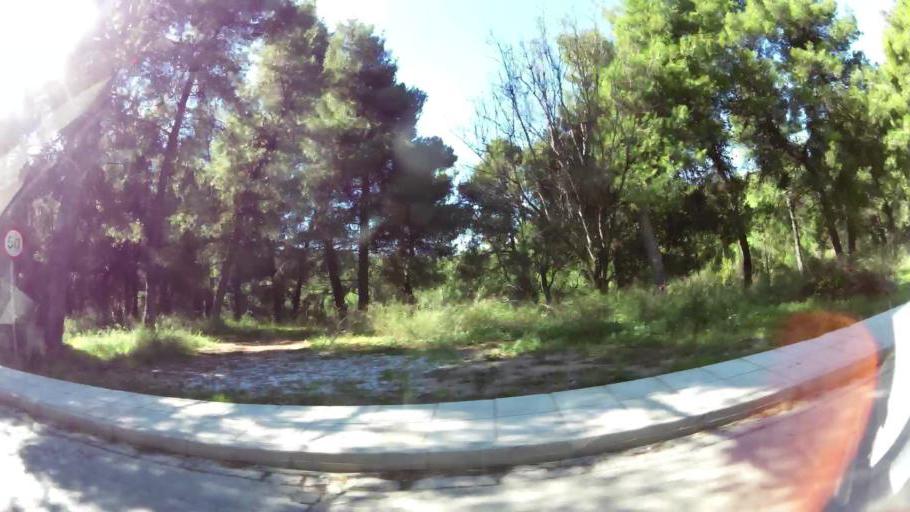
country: GR
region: Attica
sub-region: Nomarchia Anatolikis Attikis
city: Drosia
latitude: 38.1081
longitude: 23.8718
